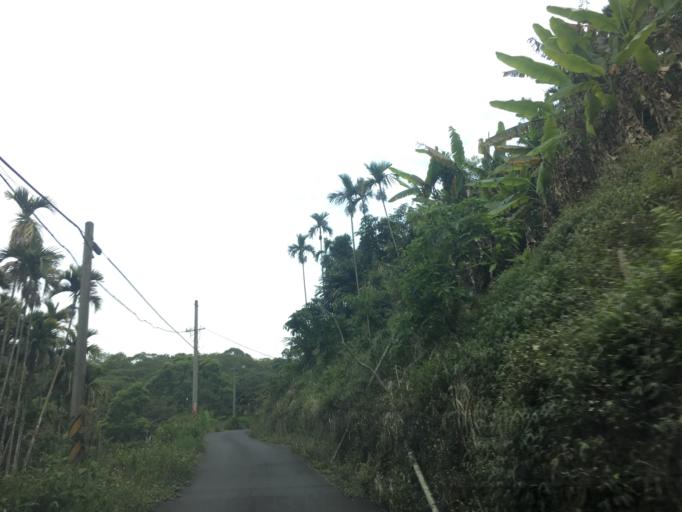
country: TW
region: Taiwan
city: Zhongxing New Village
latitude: 23.9704
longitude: 120.8243
